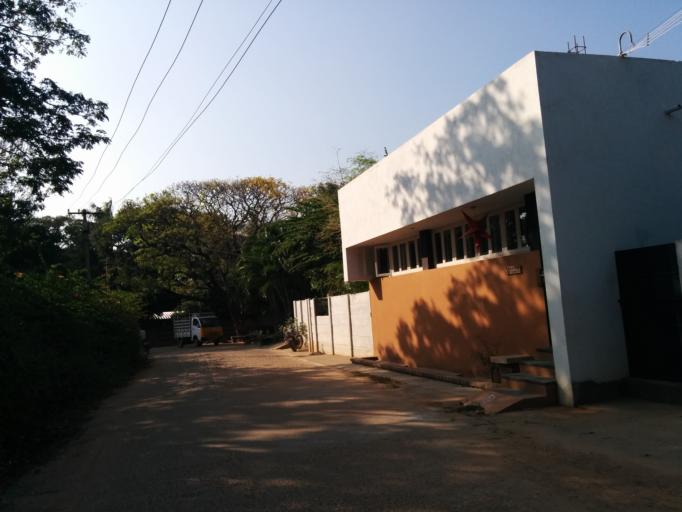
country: IN
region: Tamil Nadu
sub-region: Villupuram
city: Auroville
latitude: 11.9874
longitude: 79.8337
